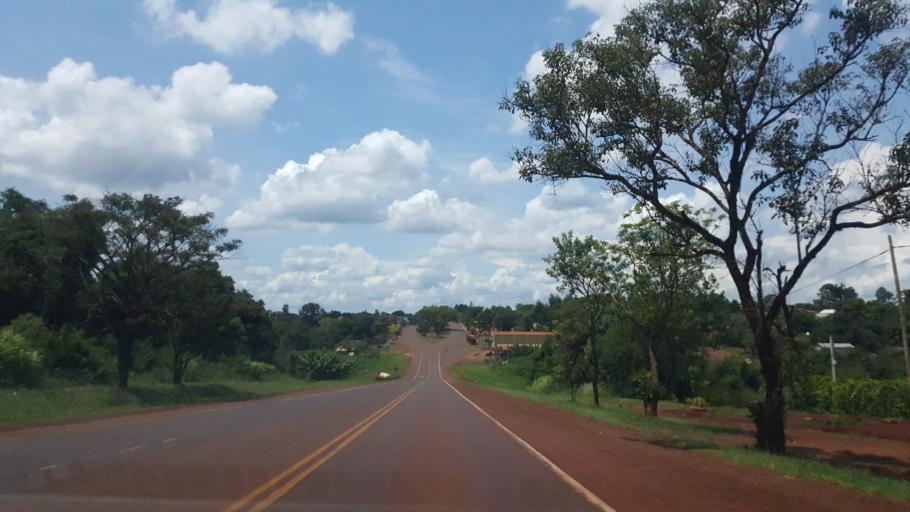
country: AR
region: Misiones
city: Garuhape
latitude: -26.8211
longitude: -54.9645
